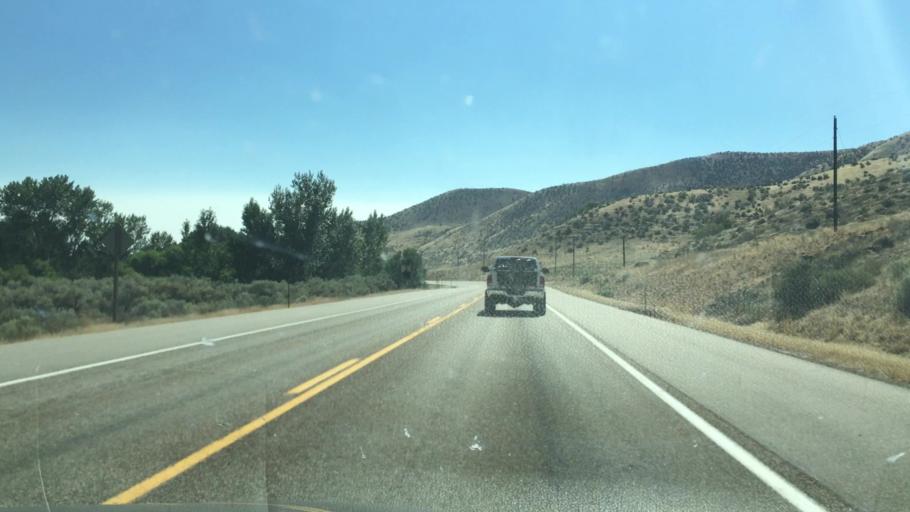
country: US
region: Idaho
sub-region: Ada County
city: Eagle
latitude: 43.7531
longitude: -116.2864
